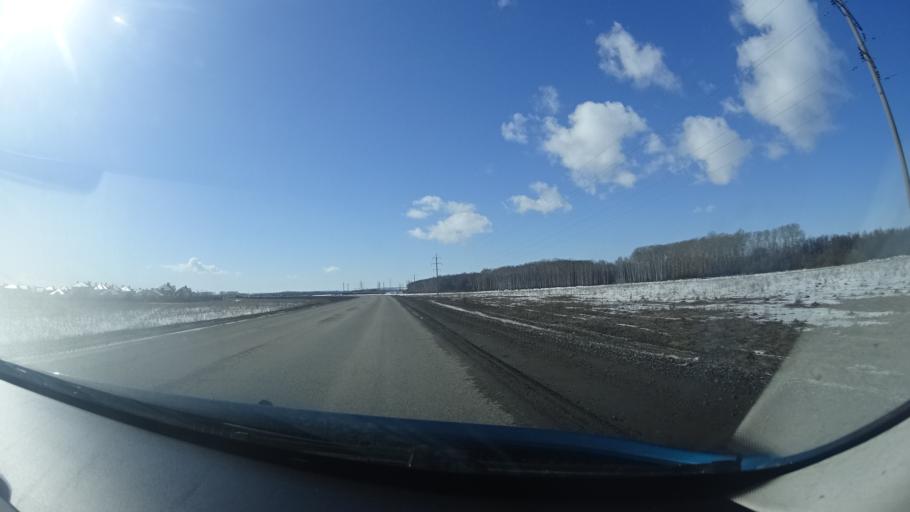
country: RU
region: Bashkortostan
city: Ufa
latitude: 54.6306
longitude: 55.9004
